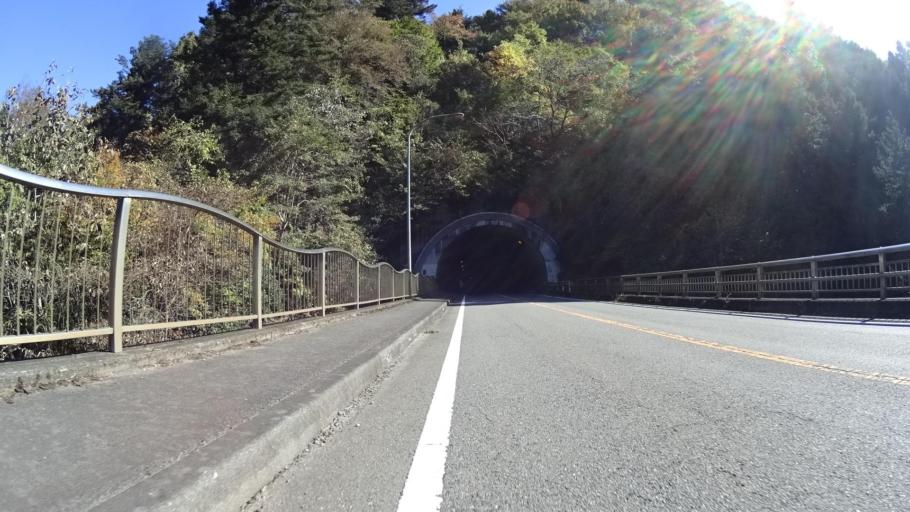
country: JP
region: Tokyo
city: Hachioji
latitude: 35.5376
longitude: 139.2505
